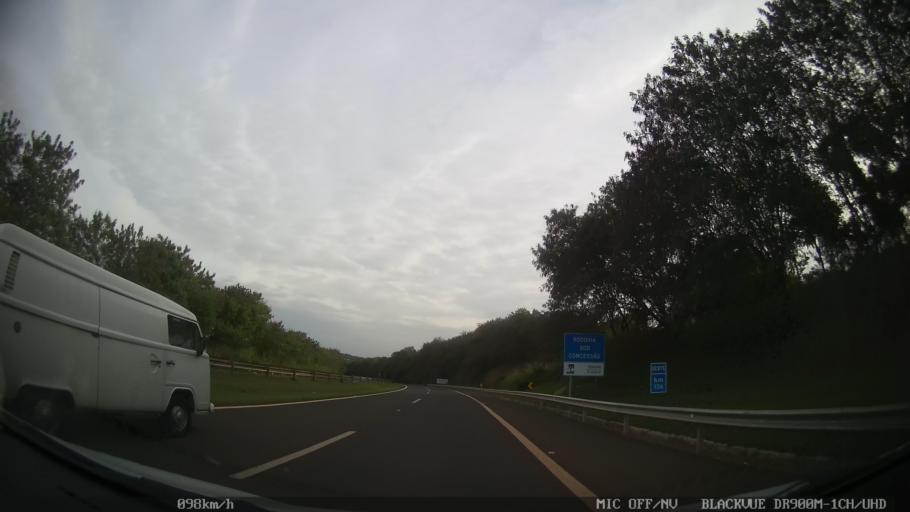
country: BR
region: Sao Paulo
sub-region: Piracicaba
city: Piracicaba
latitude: -22.6942
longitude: -47.5907
